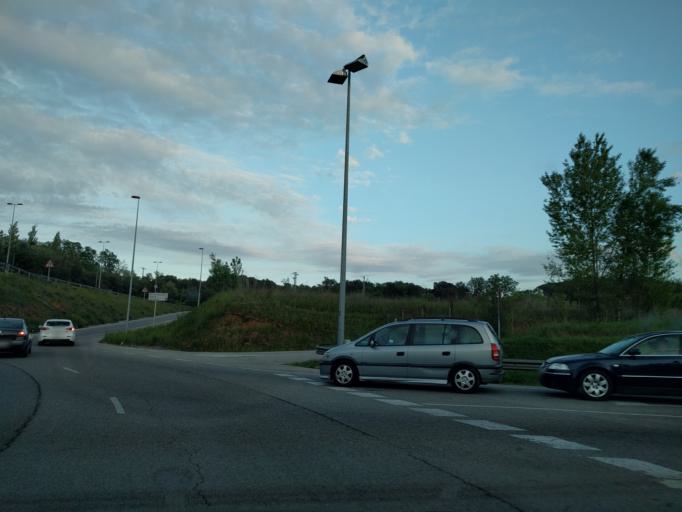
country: ES
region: Catalonia
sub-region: Provincia de Girona
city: Fornells de la Selva
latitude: 41.9562
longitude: 2.8098
